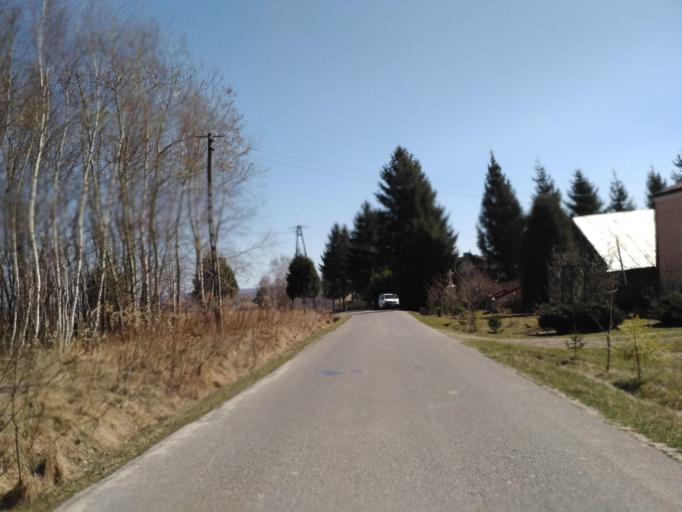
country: PL
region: Subcarpathian Voivodeship
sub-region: Powiat brzozowski
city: Orzechowka
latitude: 49.7328
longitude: 21.9317
